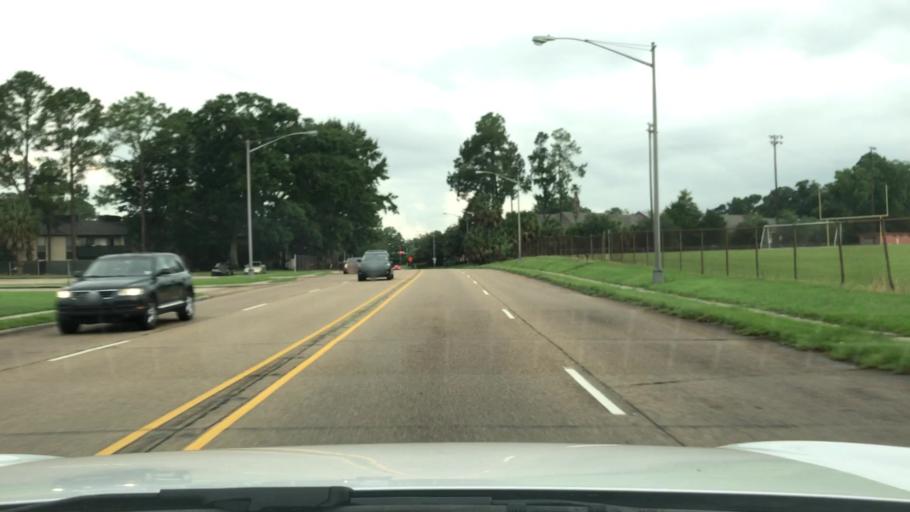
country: US
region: Louisiana
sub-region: East Baton Rouge Parish
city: Baton Rouge
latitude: 30.4395
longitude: -91.1346
